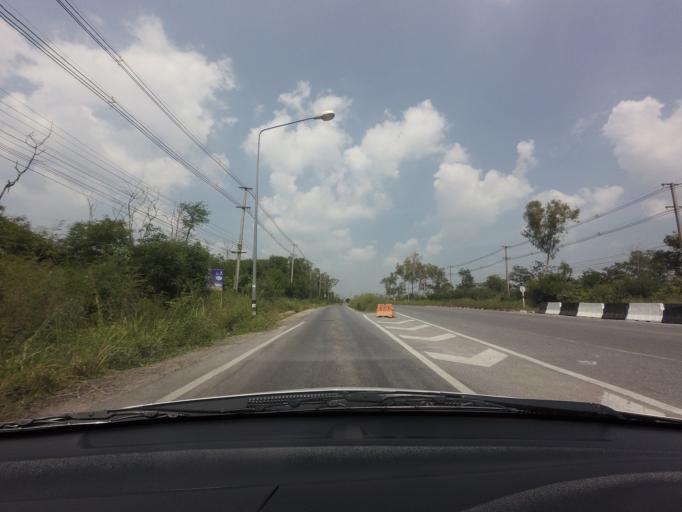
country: TH
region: Nakhon Ratchasima
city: Pak Chong
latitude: 14.6705
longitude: 101.4567
